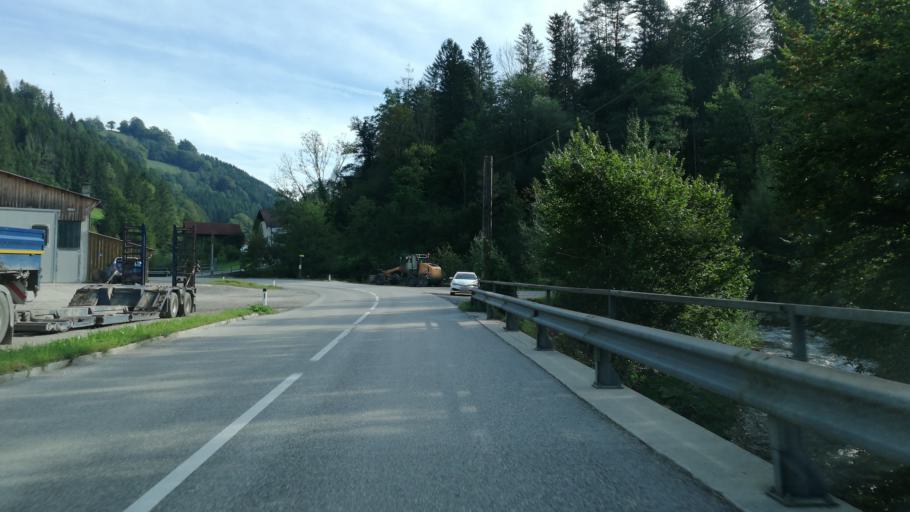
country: AT
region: Upper Austria
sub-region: Politischer Bezirk Steyr-Land
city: Maria Neustift
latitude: 47.8954
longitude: 14.5454
